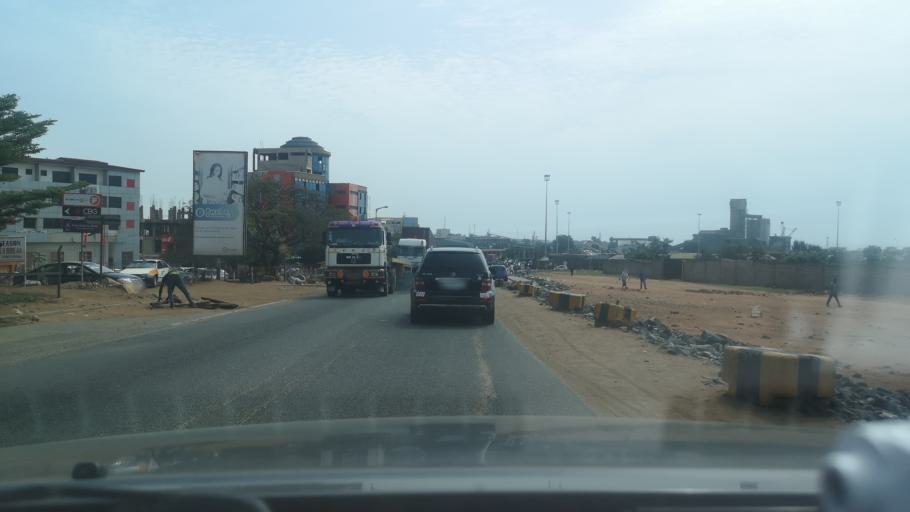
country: GH
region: Greater Accra
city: Tema
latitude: 5.6355
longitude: 0.0006
